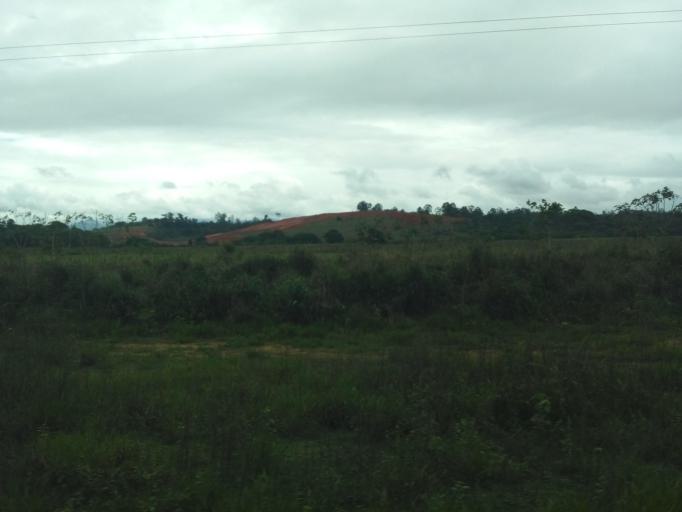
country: BR
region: Minas Gerais
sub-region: Ipatinga
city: Ipatinga
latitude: -19.4703
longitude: -42.4814
